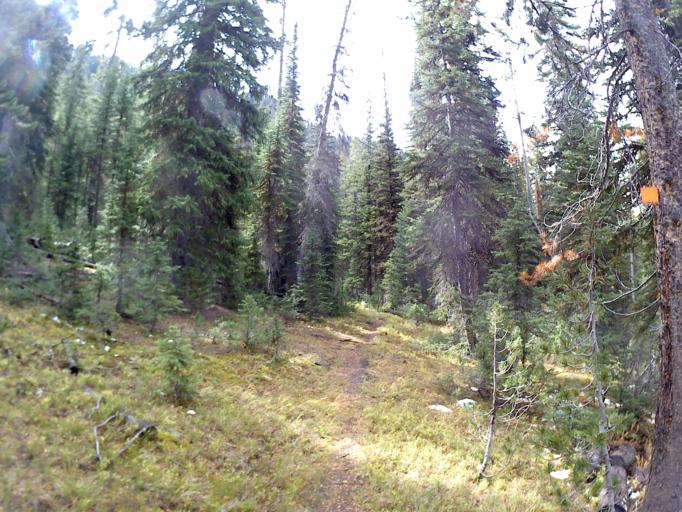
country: US
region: Montana
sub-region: Gallatin County
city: West Yellowstone
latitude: 44.4299
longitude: -110.7456
